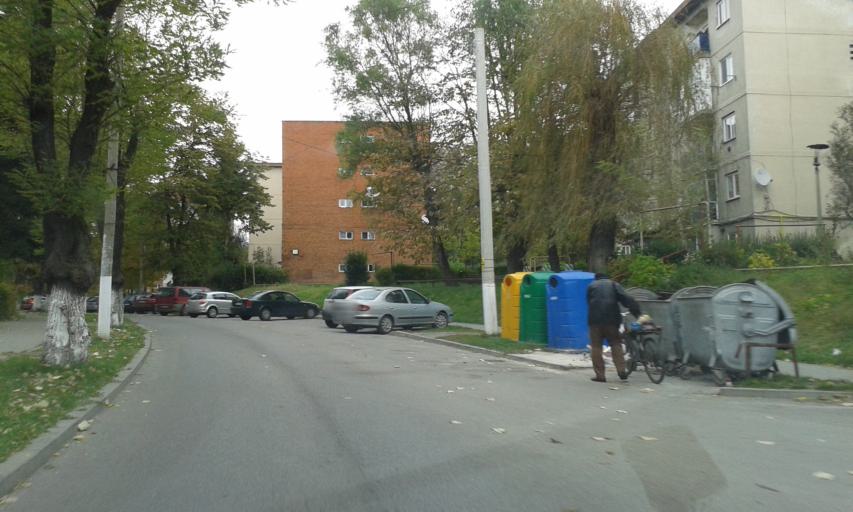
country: RO
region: Hunedoara
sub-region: Municipiul Petrosani
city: Petrosani
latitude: 45.4024
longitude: 23.3773
